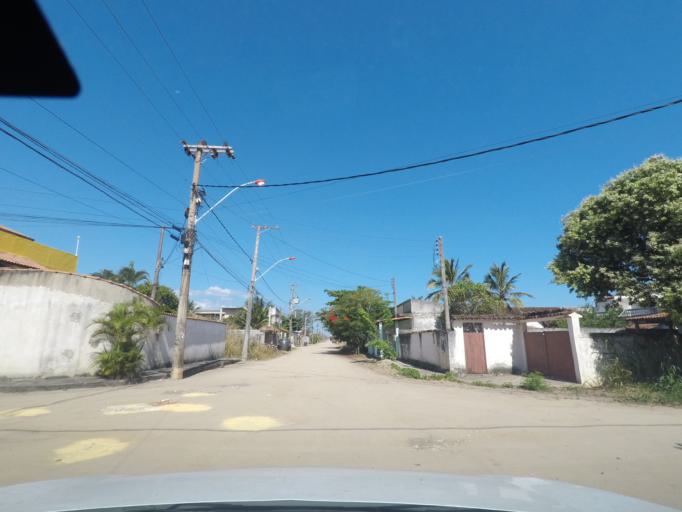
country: BR
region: Rio de Janeiro
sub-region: Marica
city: Marica
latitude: -22.9694
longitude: -42.9137
